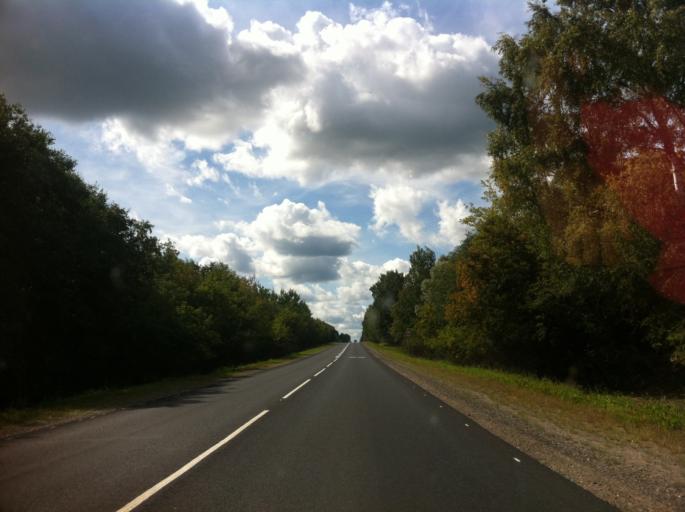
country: RU
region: Pskov
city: Izborsk
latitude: 57.7220
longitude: 27.9395
